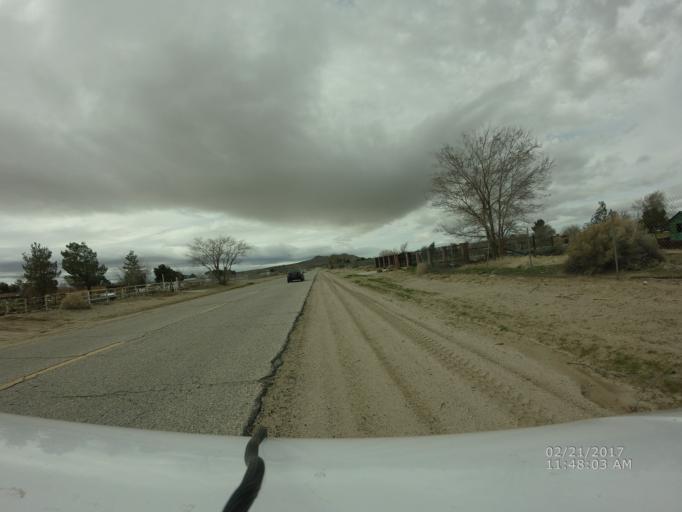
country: US
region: California
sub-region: Los Angeles County
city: Lake Los Angeles
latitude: 34.6312
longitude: -117.8465
